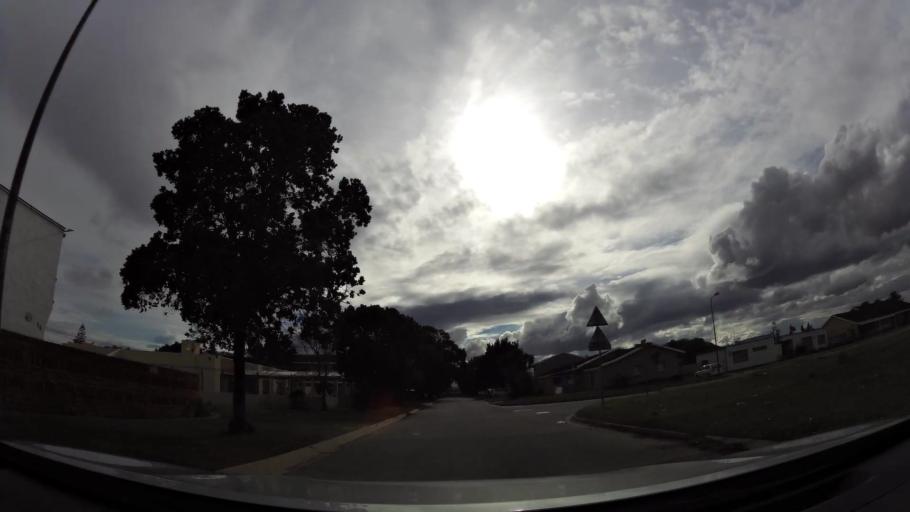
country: ZA
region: Eastern Cape
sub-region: Nelson Mandela Bay Metropolitan Municipality
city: Port Elizabeth
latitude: -33.9380
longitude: 25.5043
